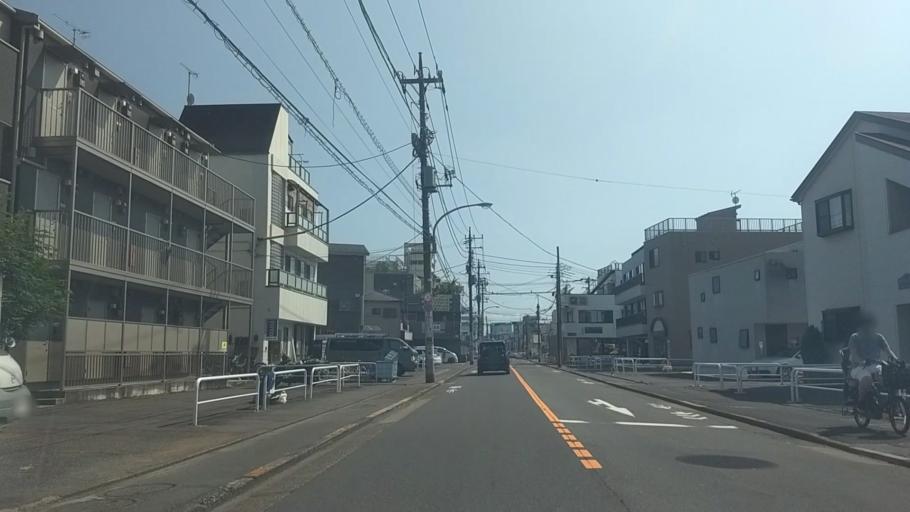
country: JP
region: Kanagawa
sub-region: Kawasaki-shi
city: Kawasaki
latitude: 35.5771
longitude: 139.7268
